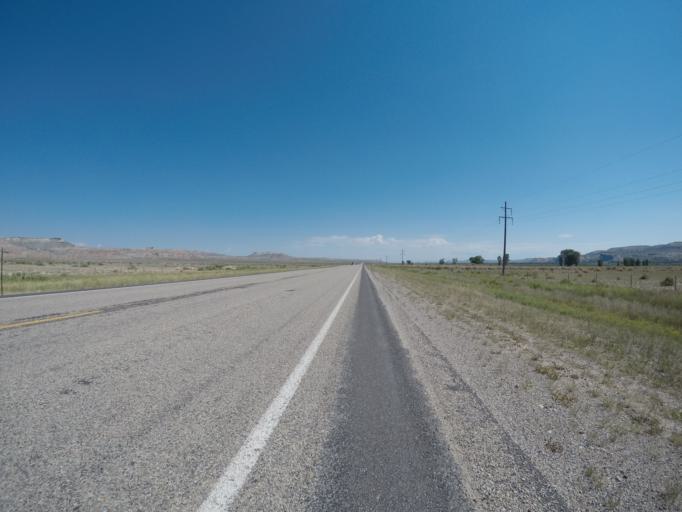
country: US
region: Wyoming
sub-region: Sublette County
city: Marbleton
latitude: 42.3362
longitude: -110.1676
